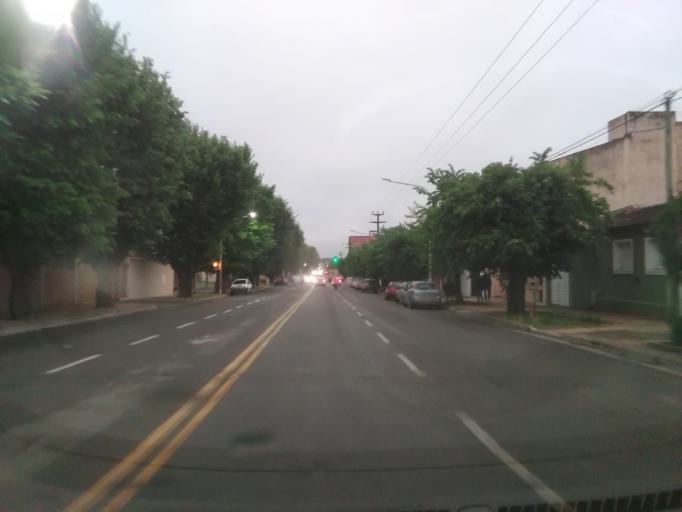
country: AR
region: Buenos Aires
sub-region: Partido de Tandil
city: Tandil
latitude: -37.3294
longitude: -59.1450
